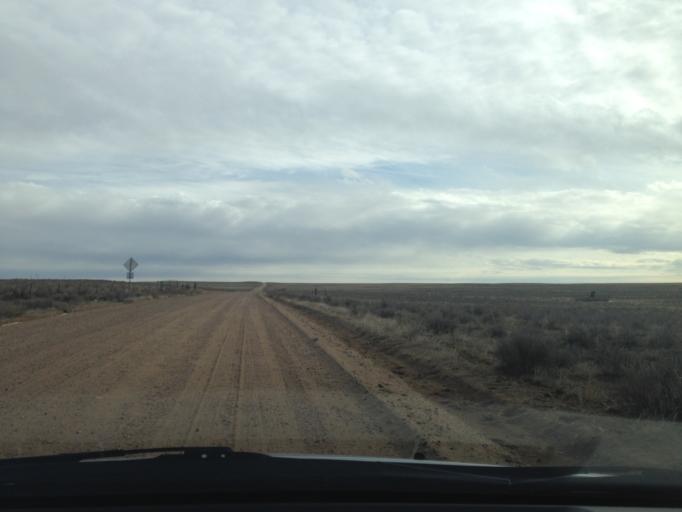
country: US
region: Colorado
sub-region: Weld County
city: Keenesburg
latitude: 40.2696
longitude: -104.2069
